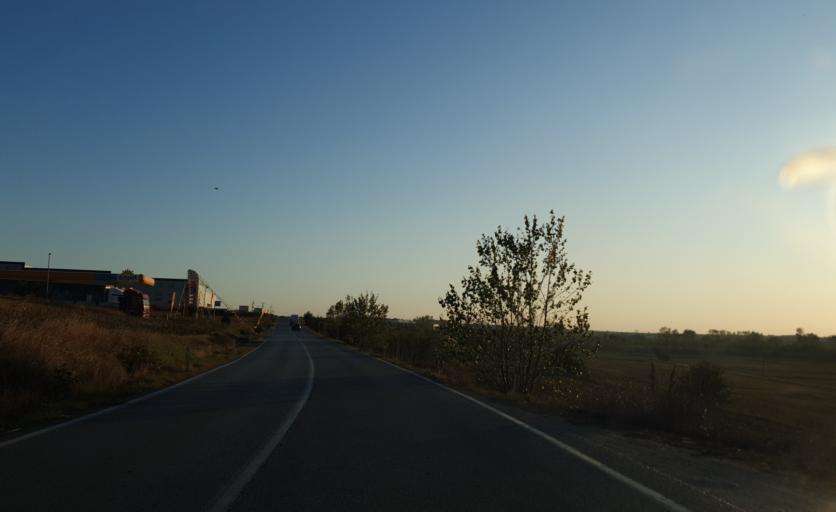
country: TR
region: Tekirdag
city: Beyazkoy
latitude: 41.3449
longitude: 27.7134
